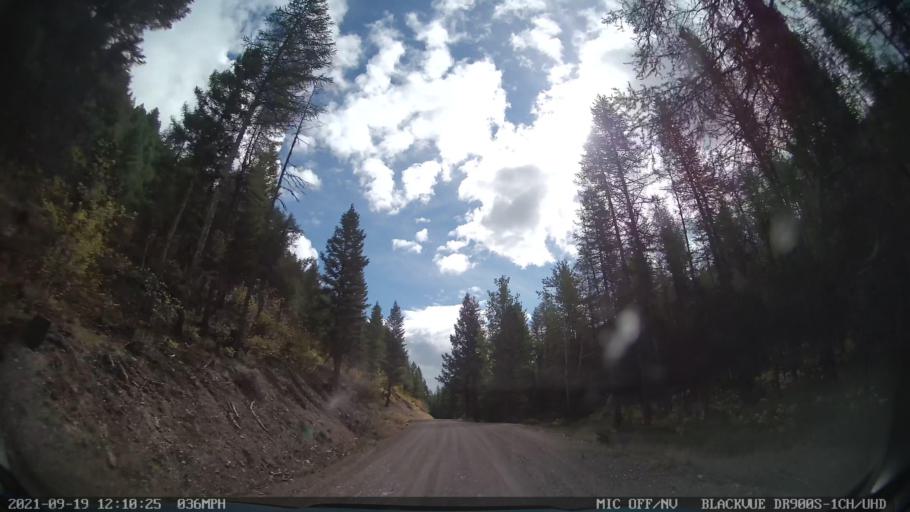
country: US
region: Montana
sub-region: Missoula County
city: Seeley Lake
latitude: 47.1790
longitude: -113.3835
